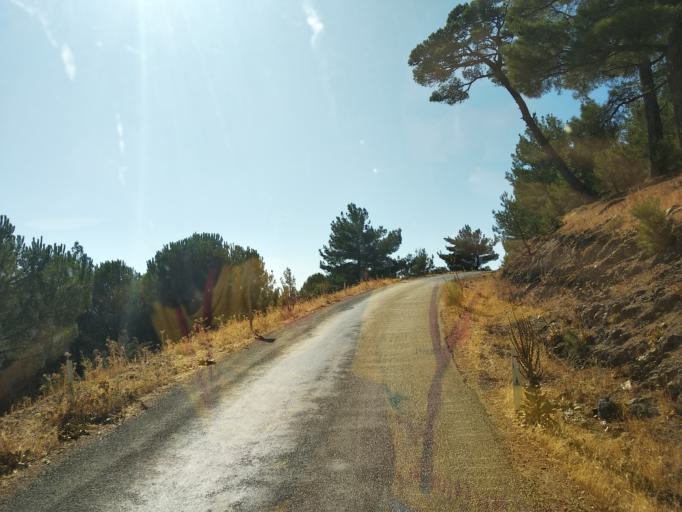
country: TR
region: Izmir
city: Gaziemir
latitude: 38.2989
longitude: 26.9966
